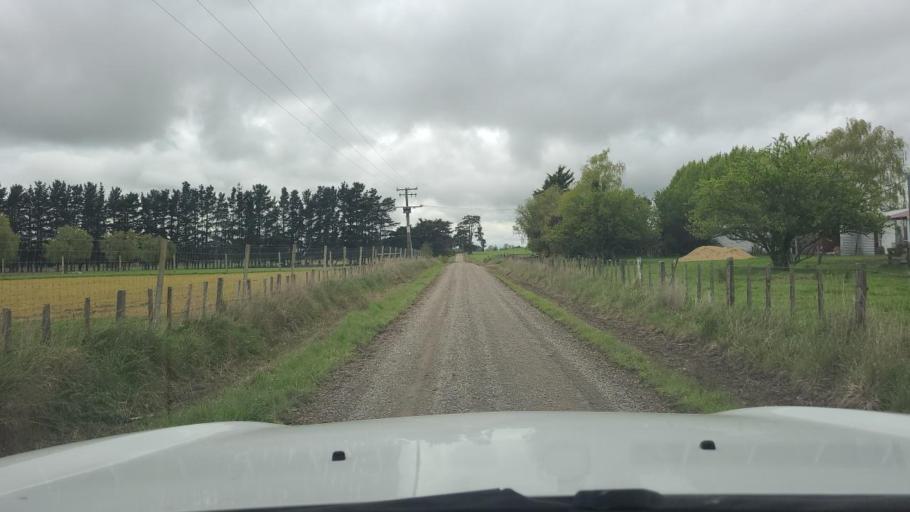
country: NZ
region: Wellington
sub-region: Masterton District
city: Masterton
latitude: -41.0519
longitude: 175.5212
